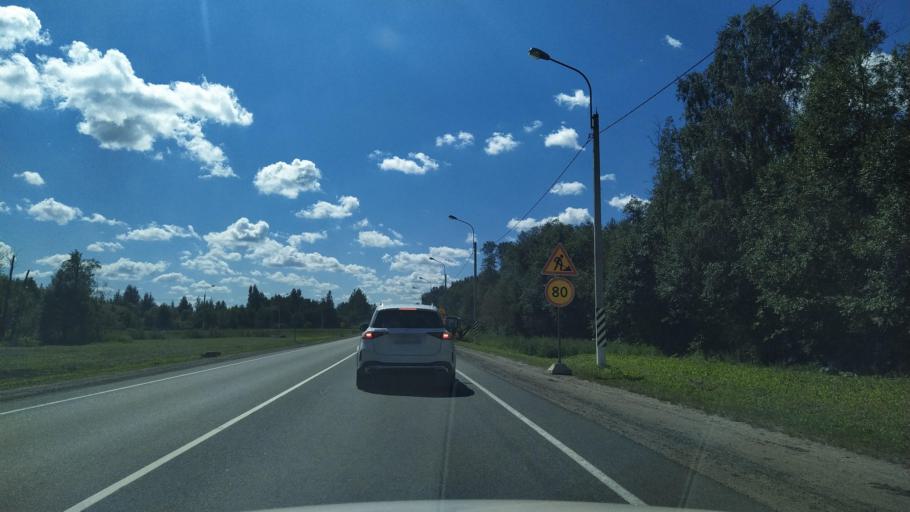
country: RU
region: Leningrad
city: Luga
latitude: 58.6221
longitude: 29.8322
